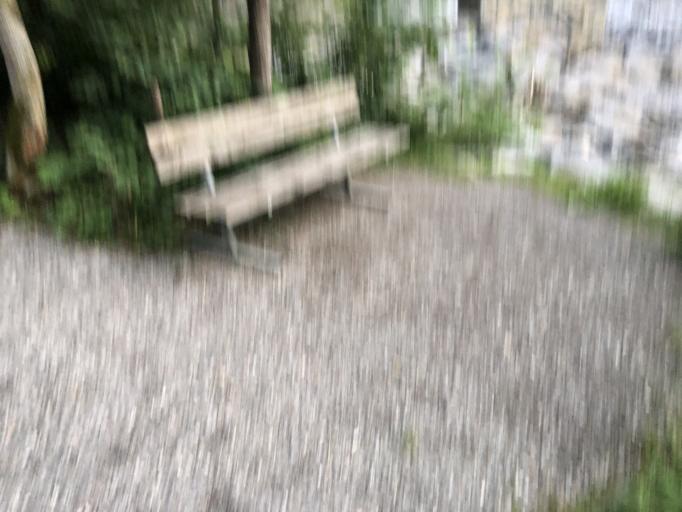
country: AT
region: Vorarlberg
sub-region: Politischer Bezirk Bregenz
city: Reuthe
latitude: 47.3451
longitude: 9.8706
